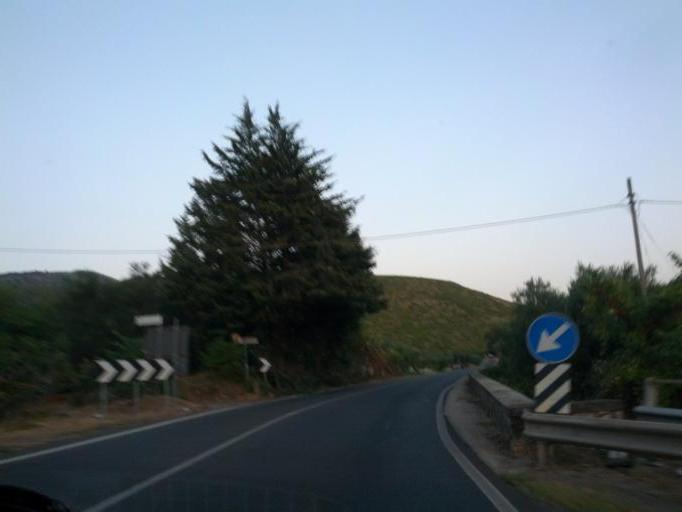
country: IT
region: Latium
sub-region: Provincia di Latina
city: Fondi
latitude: 41.3245
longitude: 13.4770
